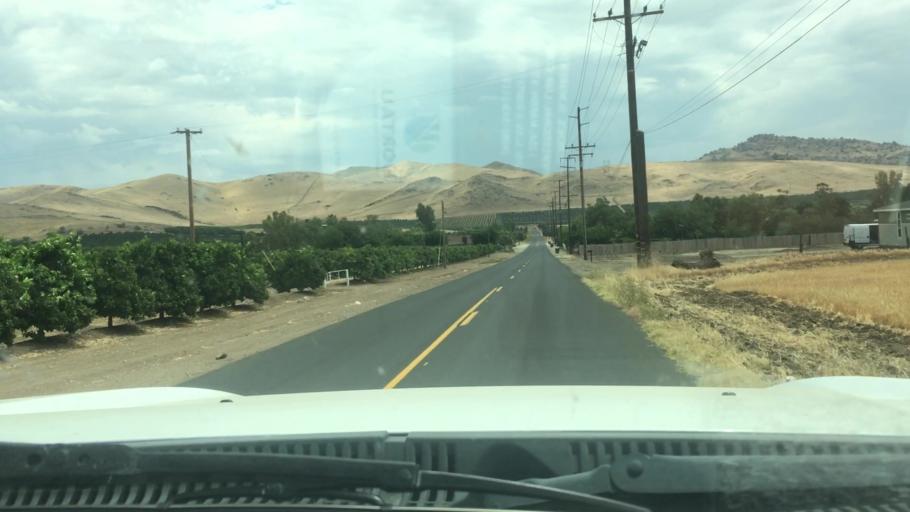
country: US
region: California
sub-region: Tulare County
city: Porterville
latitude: 36.0964
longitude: -119.0229
